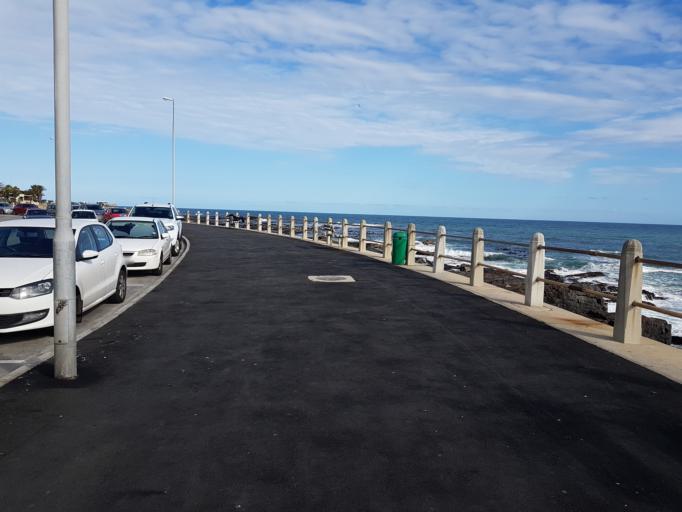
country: ZA
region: Western Cape
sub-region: City of Cape Town
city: Cape Town
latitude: -33.9189
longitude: 18.3825
